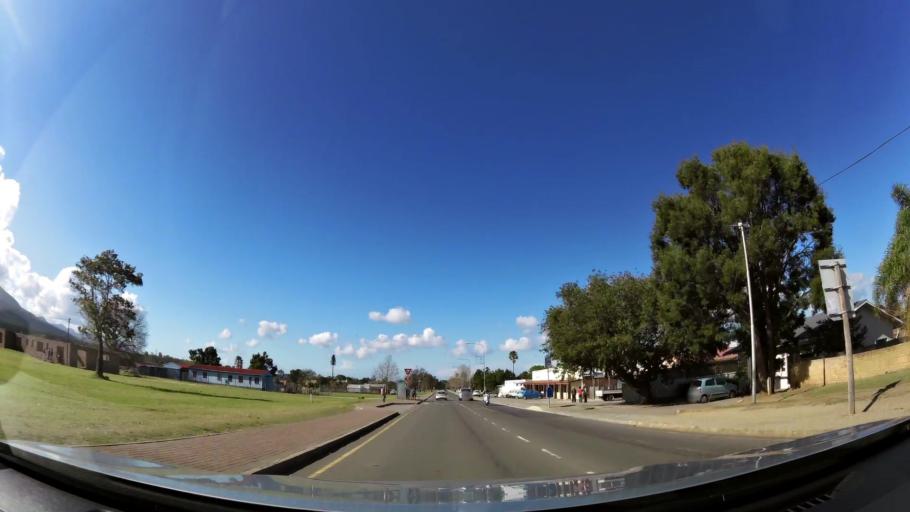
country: ZA
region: Western Cape
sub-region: Eden District Municipality
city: George
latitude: -33.9444
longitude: 22.4143
